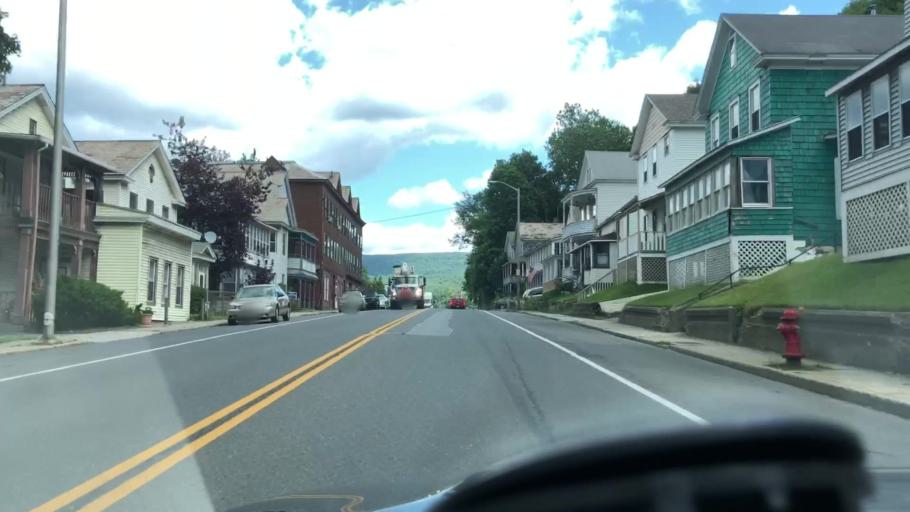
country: US
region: Massachusetts
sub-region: Berkshire County
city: North Adams
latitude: 42.7004
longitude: -73.1182
